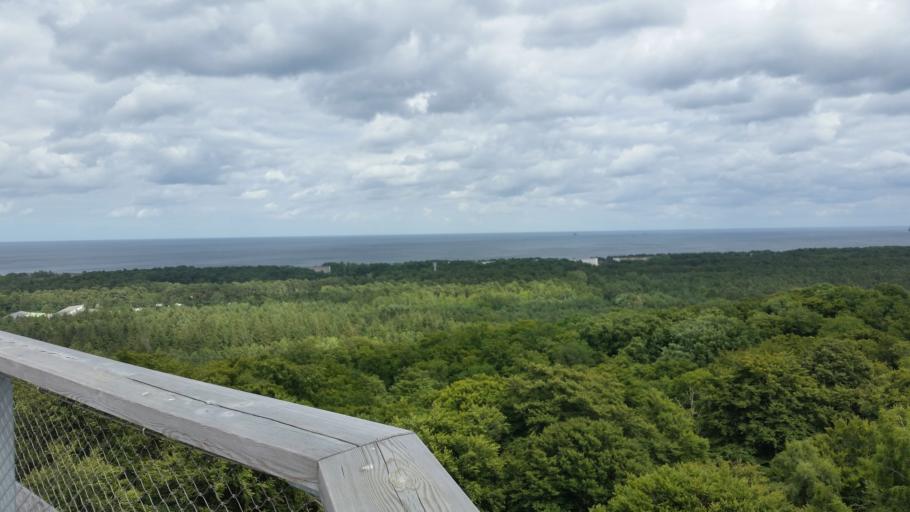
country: DE
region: Mecklenburg-Vorpommern
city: Ostseebad Binz
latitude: 54.4319
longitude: 13.5575
